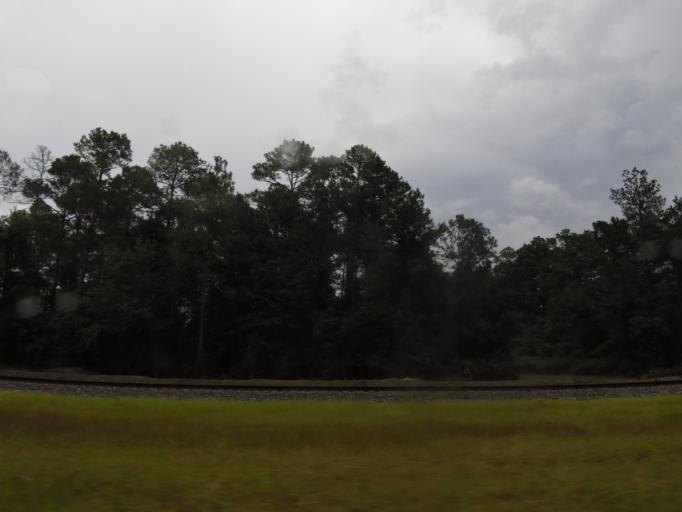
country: US
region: Georgia
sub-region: Wayne County
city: Jesup
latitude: 31.4832
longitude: -81.7352
